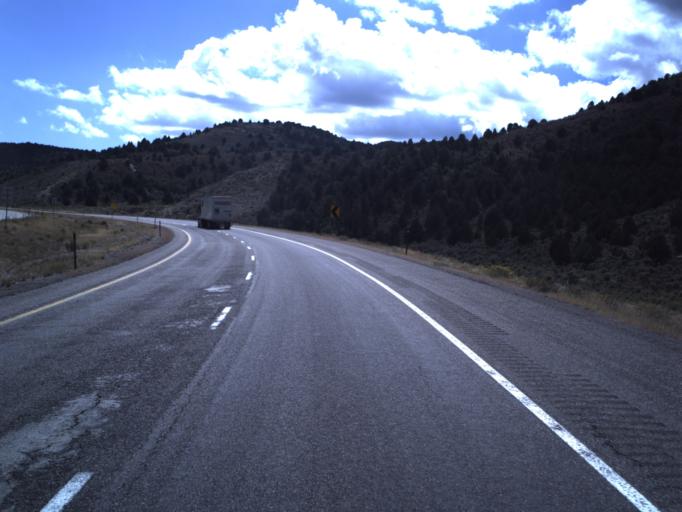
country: US
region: Utah
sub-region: Sevier County
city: Salina
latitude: 38.8128
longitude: -111.5365
